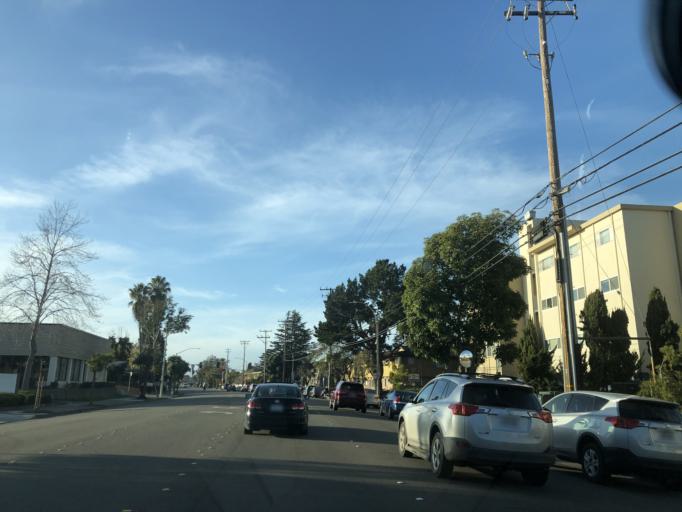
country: US
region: California
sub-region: Alameda County
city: Alameda
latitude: 37.7600
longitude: -122.2525
